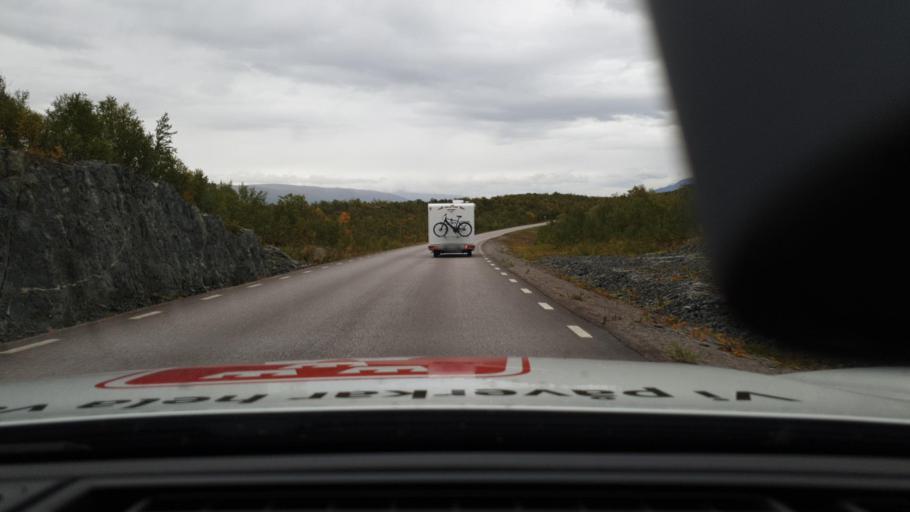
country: NO
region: Troms
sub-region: Bardu
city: Setermoen
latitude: 68.4429
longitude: 18.6198
